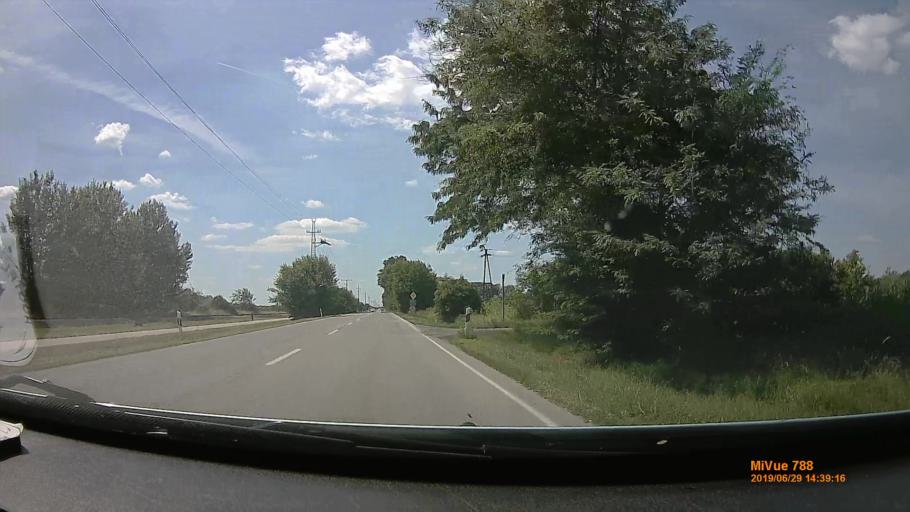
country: HU
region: Komarom-Esztergom
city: Tat
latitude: 47.7531
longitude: 18.6078
